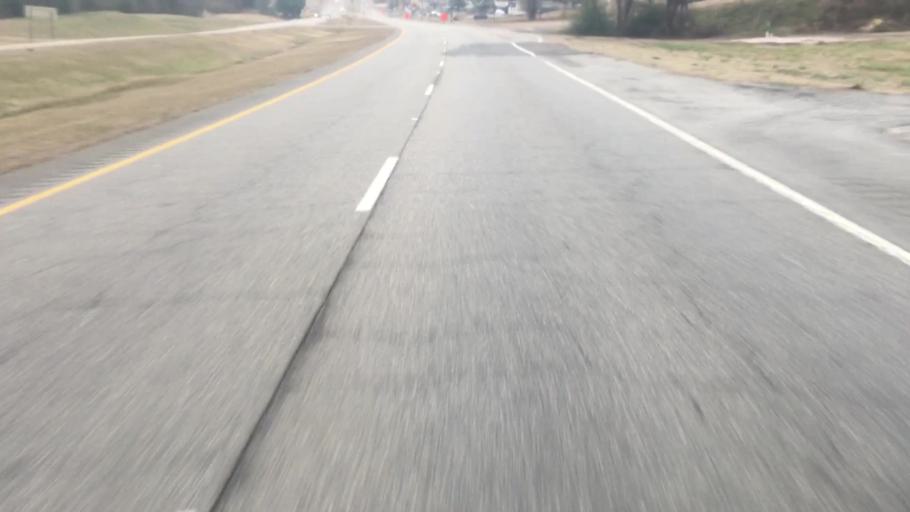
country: US
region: Alabama
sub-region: Walker County
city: Sumiton
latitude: 33.7624
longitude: -87.0684
